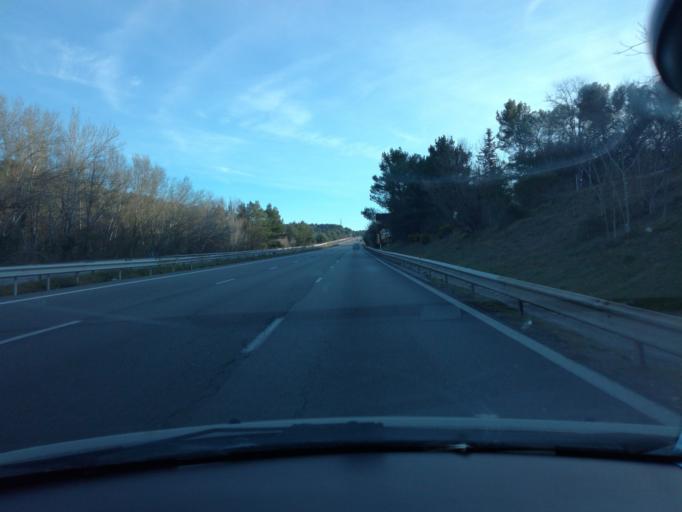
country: FR
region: Provence-Alpes-Cote d'Azur
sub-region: Departement des Bouches-du-Rhone
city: Fuveau
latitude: 43.4690
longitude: 5.5664
